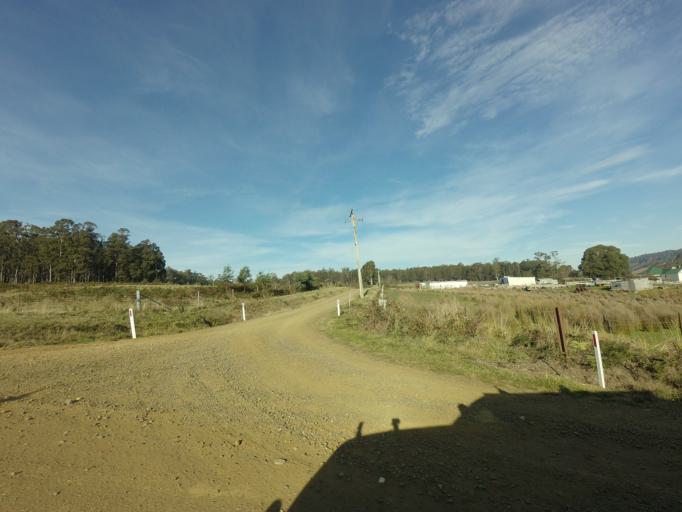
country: AU
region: Tasmania
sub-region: Brighton
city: Bridgewater
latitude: -42.4614
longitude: 147.3780
